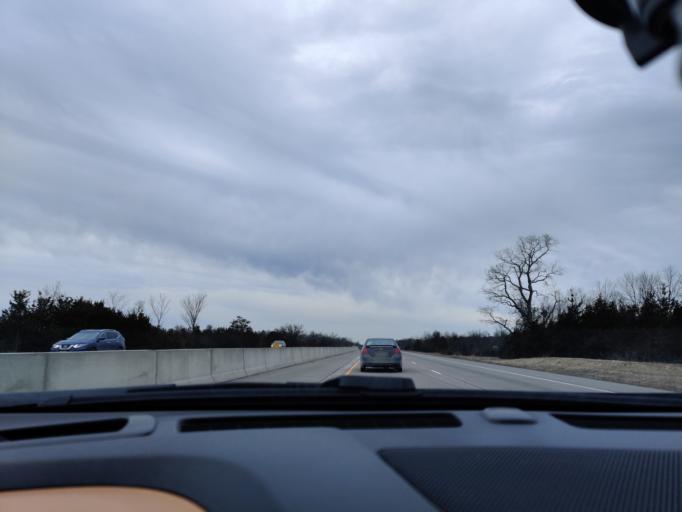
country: CA
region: Ontario
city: Deseronto
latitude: 44.2254
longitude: -77.2022
